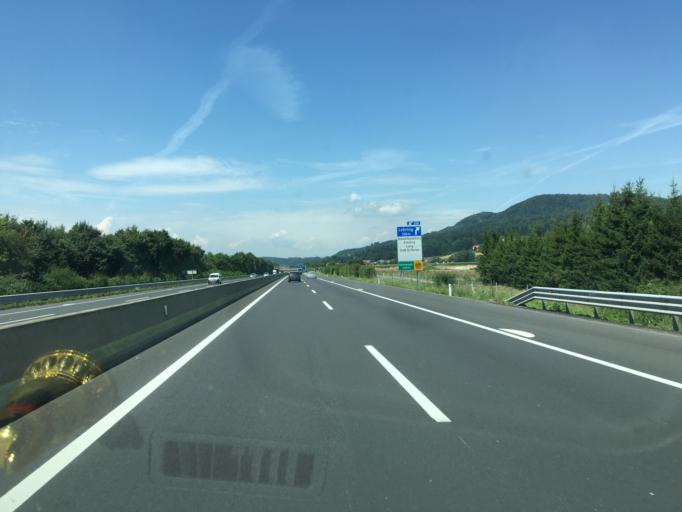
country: AT
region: Styria
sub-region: Politischer Bezirk Leibnitz
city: Lang
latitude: 46.8479
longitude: 15.5244
